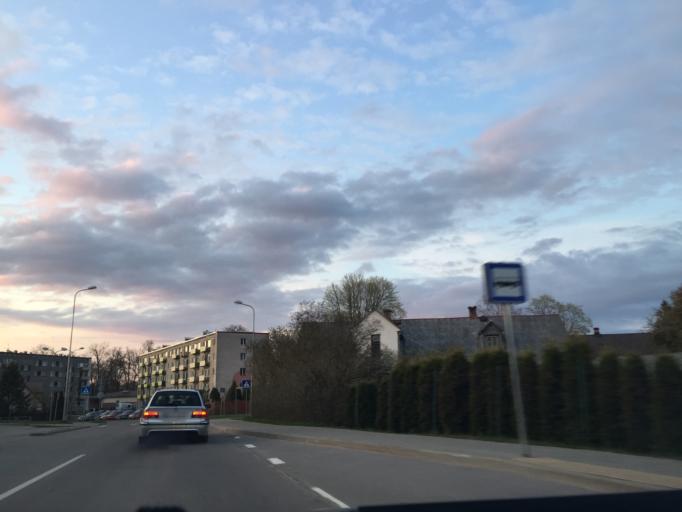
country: LV
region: Aluksnes Rajons
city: Aluksne
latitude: 57.4243
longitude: 27.0404
